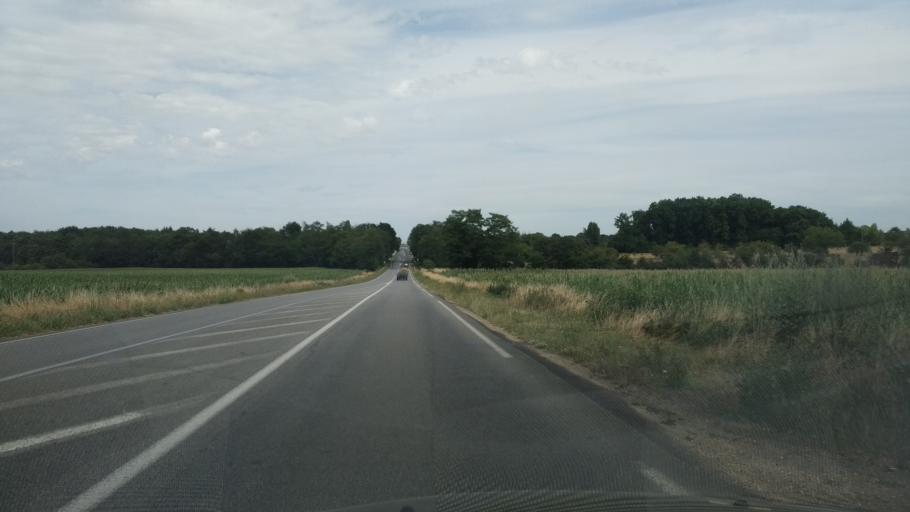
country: FR
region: Poitou-Charentes
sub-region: Departement de la Vienne
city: Mignaloux-Beauvoir
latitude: 46.5623
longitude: 0.4224
